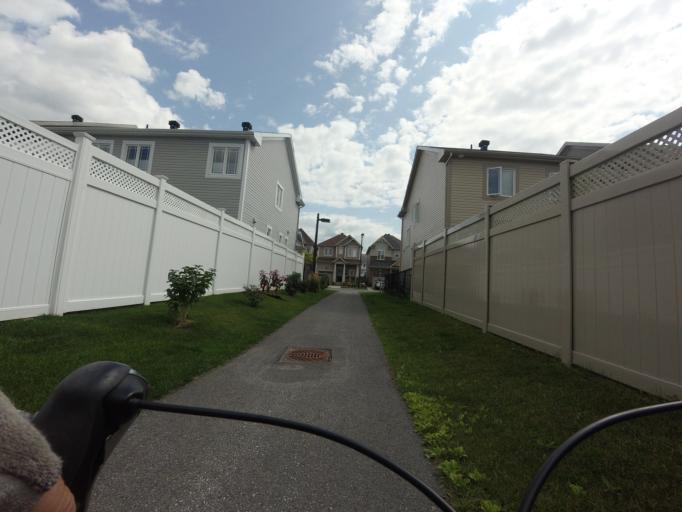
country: CA
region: Ontario
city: Bells Corners
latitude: 45.2748
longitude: -75.8489
